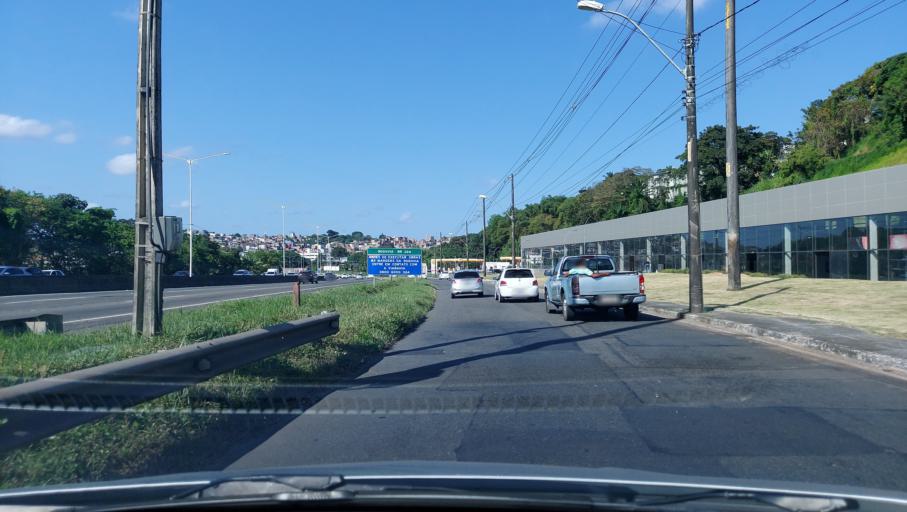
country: BR
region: Bahia
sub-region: Salvador
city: Salvador
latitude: -12.9609
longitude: -38.4744
